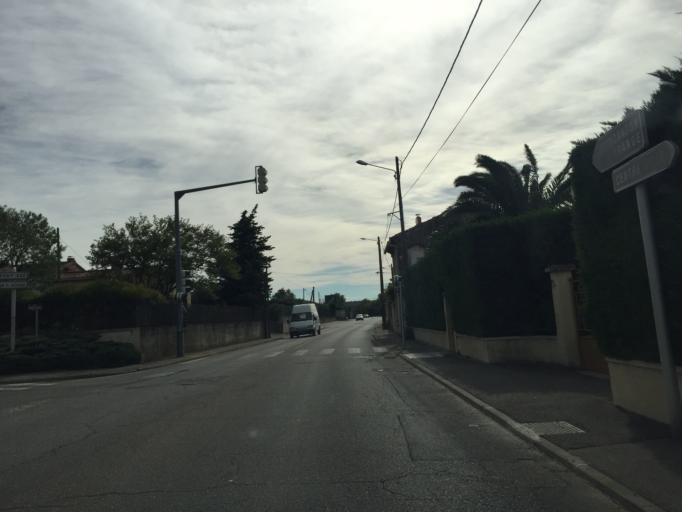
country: FR
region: Provence-Alpes-Cote d'Azur
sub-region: Departement du Vaucluse
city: Bollene
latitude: 44.2742
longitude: 4.7441
